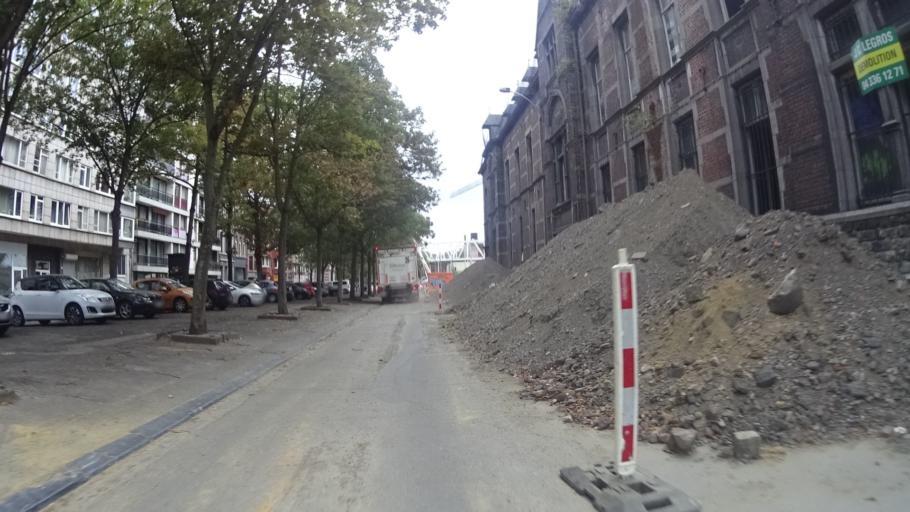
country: BE
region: Wallonia
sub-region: Province de Liege
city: Liege
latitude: 50.6439
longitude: 5.5876
